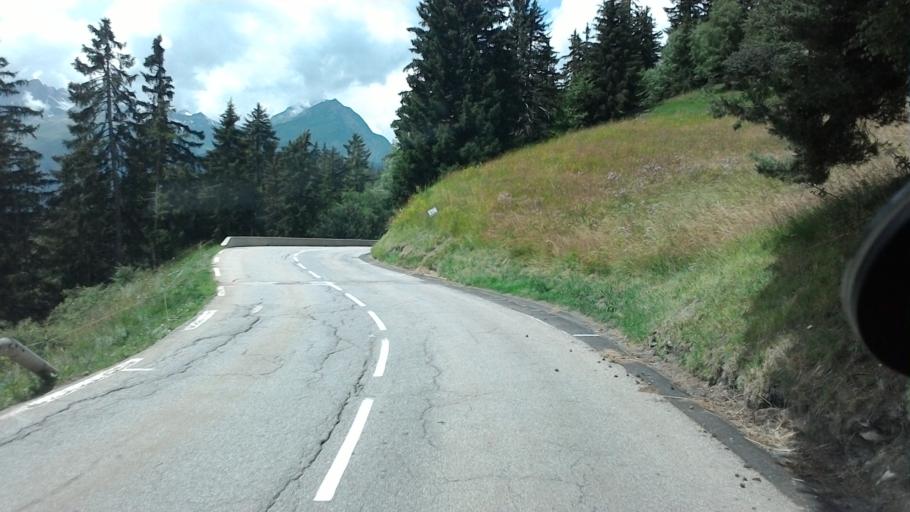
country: FR
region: Rhone-Alpes
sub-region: Departement de la Savoie
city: Seez
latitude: 45.6219
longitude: 6.8462
